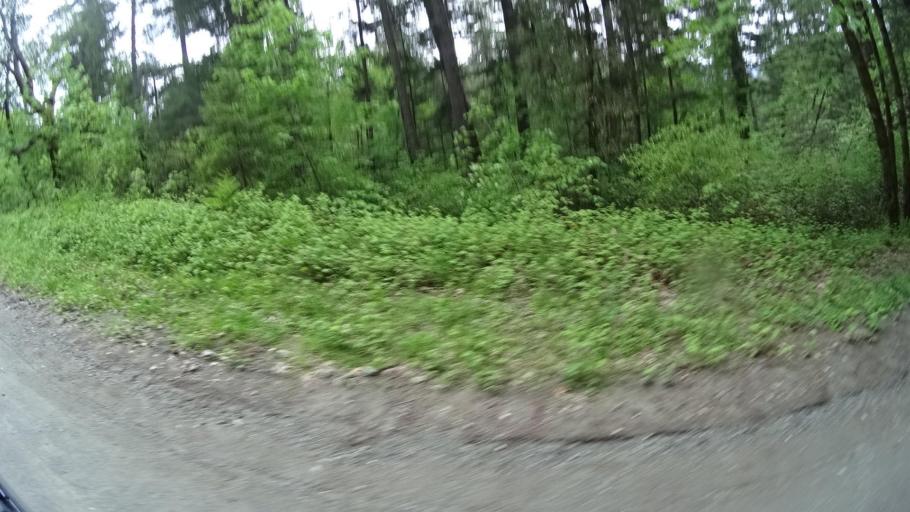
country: US
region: California
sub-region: Humboldt County
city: Willow Creek
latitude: 41.1248
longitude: -123.7479
